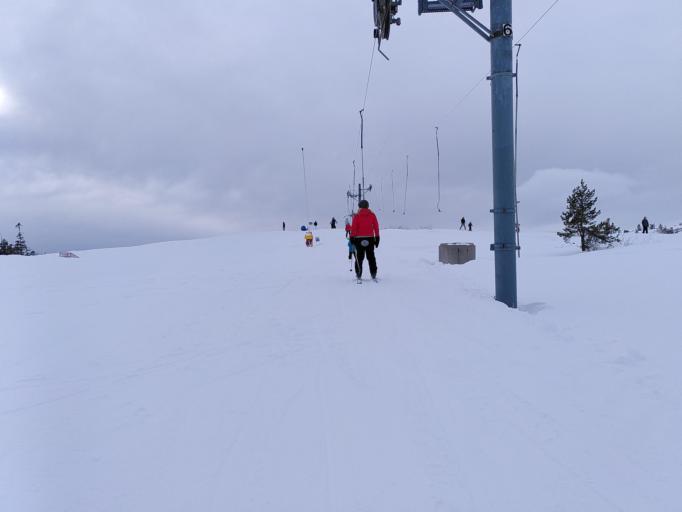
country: NO
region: Buskerud
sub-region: Flesberg
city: Lampeland
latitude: 59.8001
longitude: 9.3881
